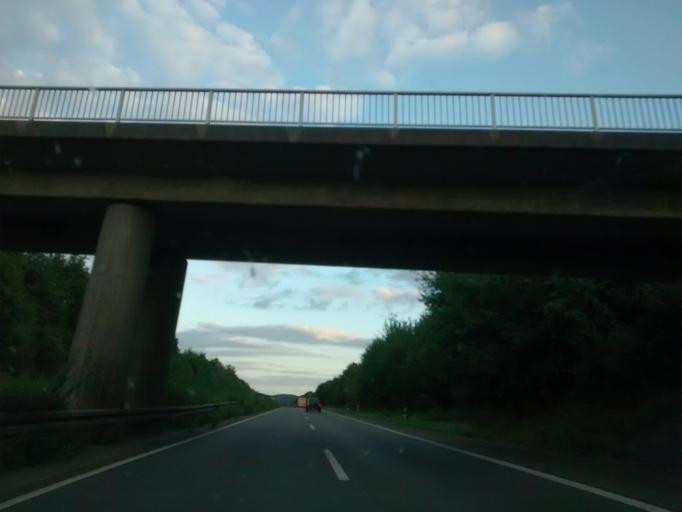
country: DE
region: Lower Saxony
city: Bissendorf
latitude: 52.2177
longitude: 8.1099
